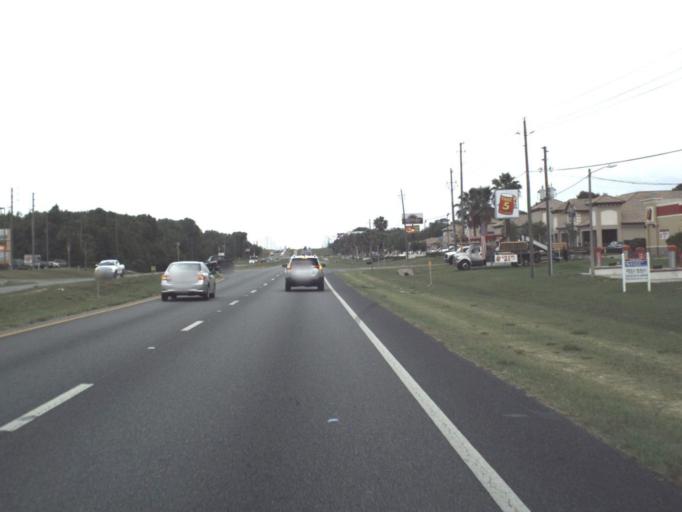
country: US
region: Florida
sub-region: Sumter County
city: The Villages
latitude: 28.9790
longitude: -81.9847
